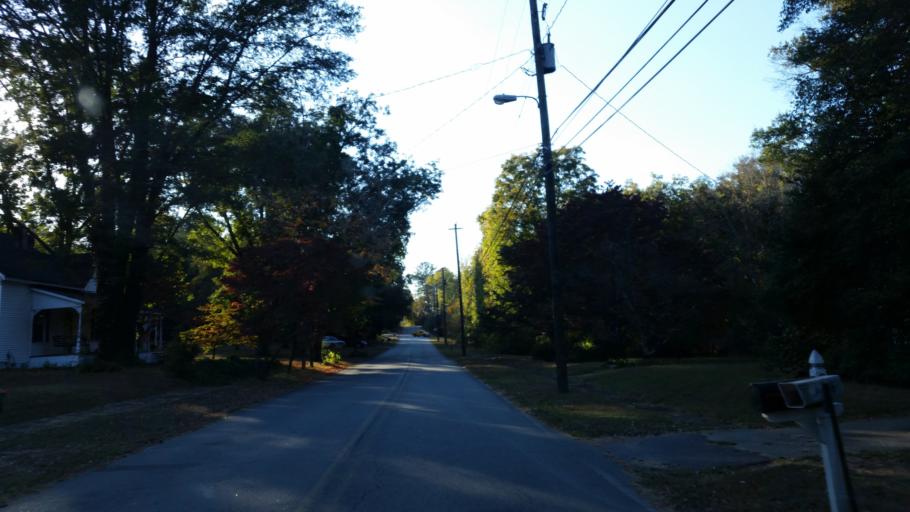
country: US
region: Georgia
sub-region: Bartow County
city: Euharlee
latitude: 34.2352
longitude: -84.9416
